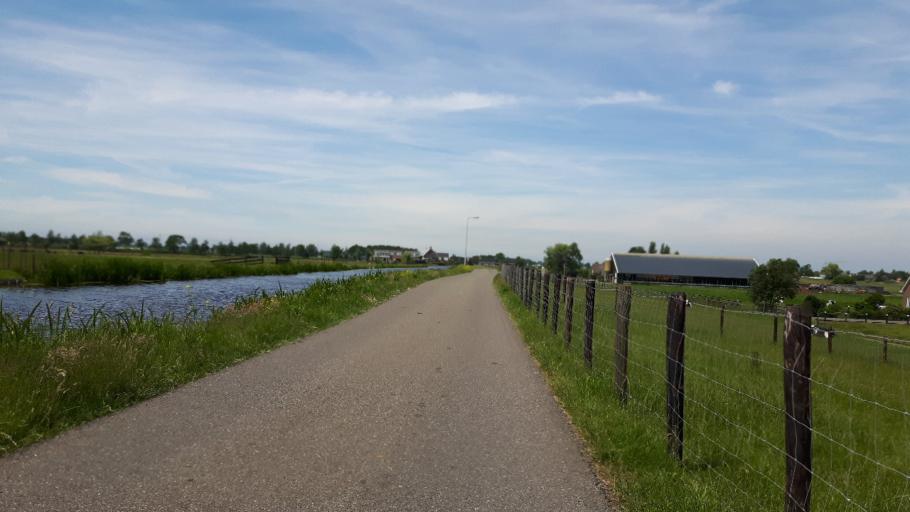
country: NL
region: South Holland
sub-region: Gemeente Nieuwkoop
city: Nieuwkoop
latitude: 52.1526
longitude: 4.7267
